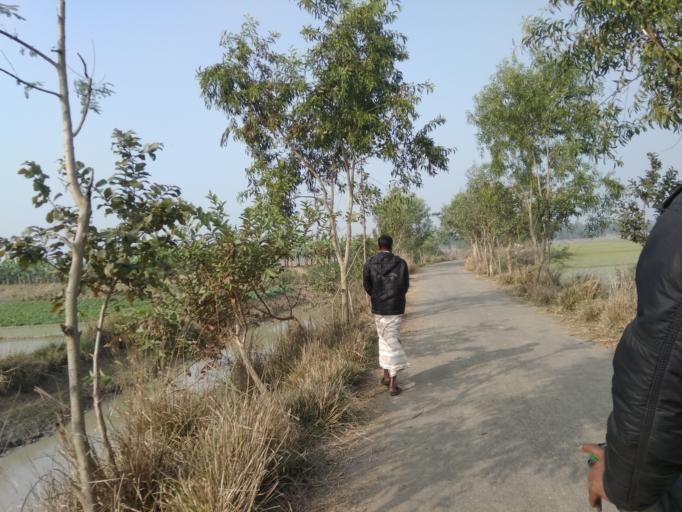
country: BD
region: Rajshahi
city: Bogra
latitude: 24.4718
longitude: 89.2686
